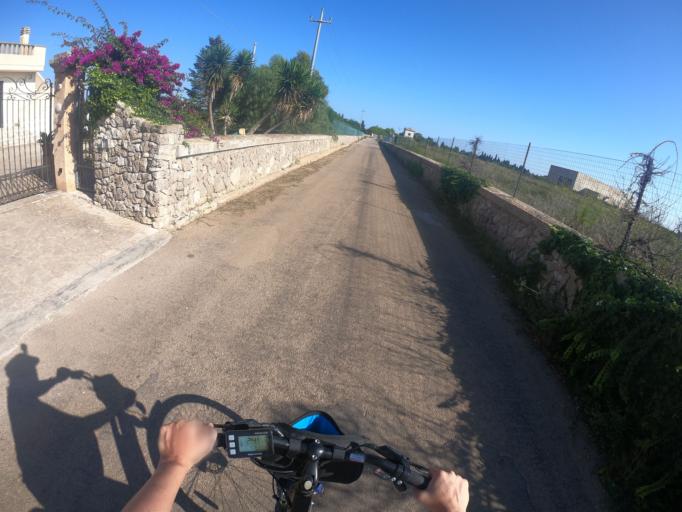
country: IT
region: Apulia
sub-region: Provincia di Lecce
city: Alessano
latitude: 39.8854
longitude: 18.3277
